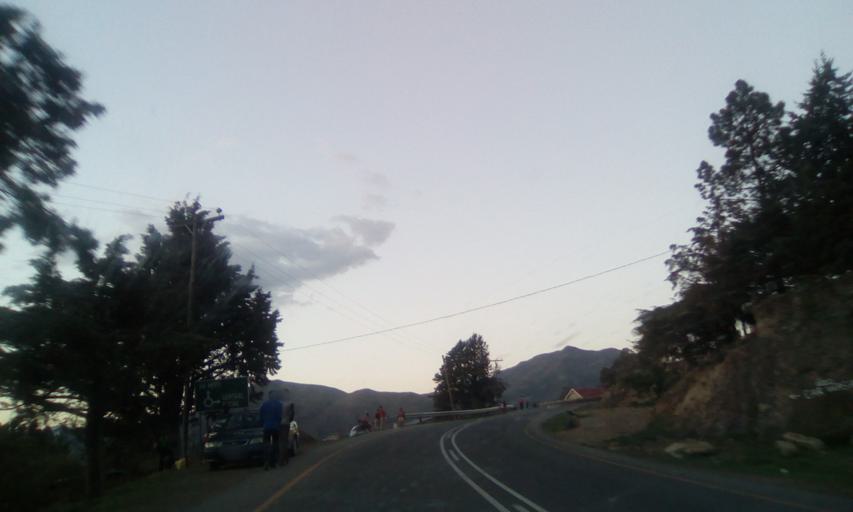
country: LS
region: Qacha's Nek
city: Qacha's Nek
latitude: -30.1211
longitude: 28.6860
